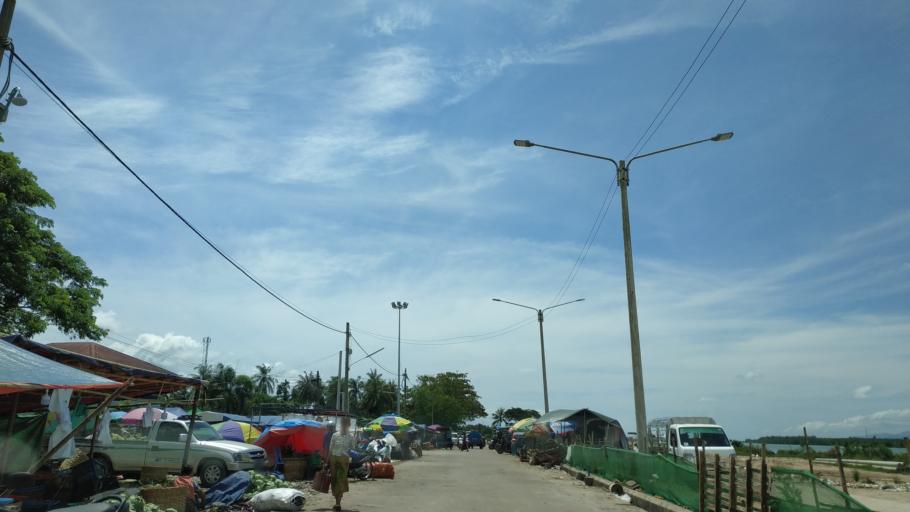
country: MM
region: Tanintharyi
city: Dawei
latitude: 14.0726
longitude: 98.1849
